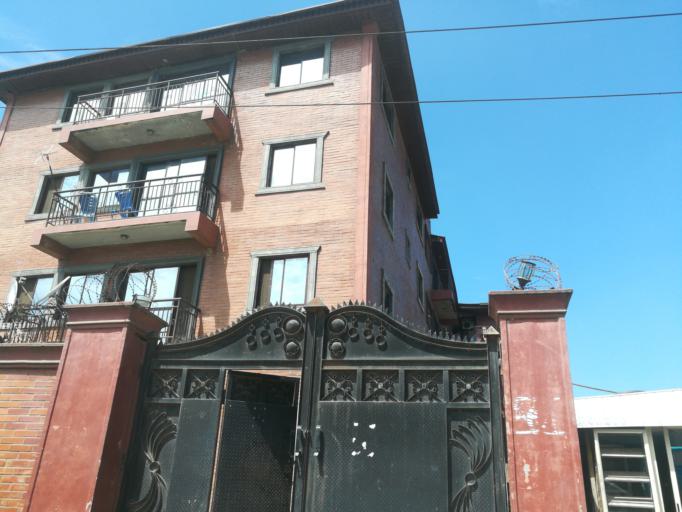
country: NG
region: Lagos
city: Oshodi
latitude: 6.5618
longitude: 3.3339
